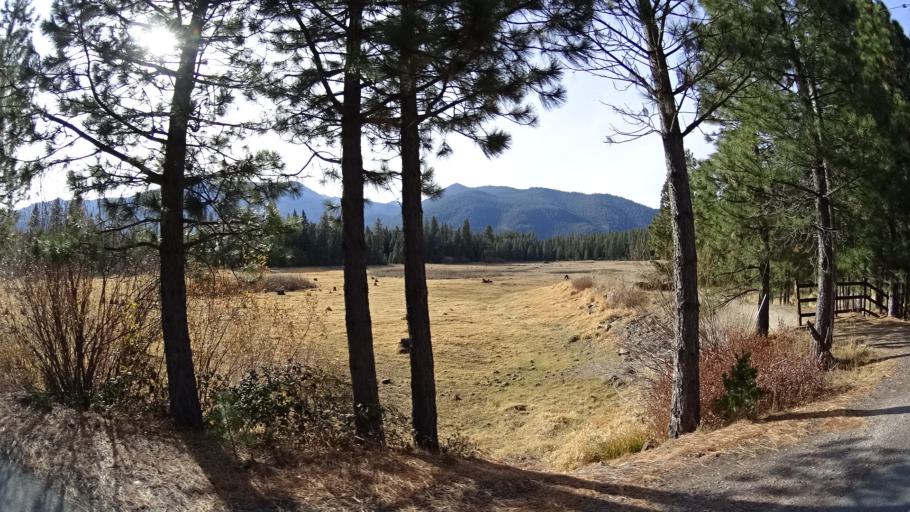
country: US
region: California
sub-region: Siskiyou County
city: Weed
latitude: 41.3857
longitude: -122.4090
